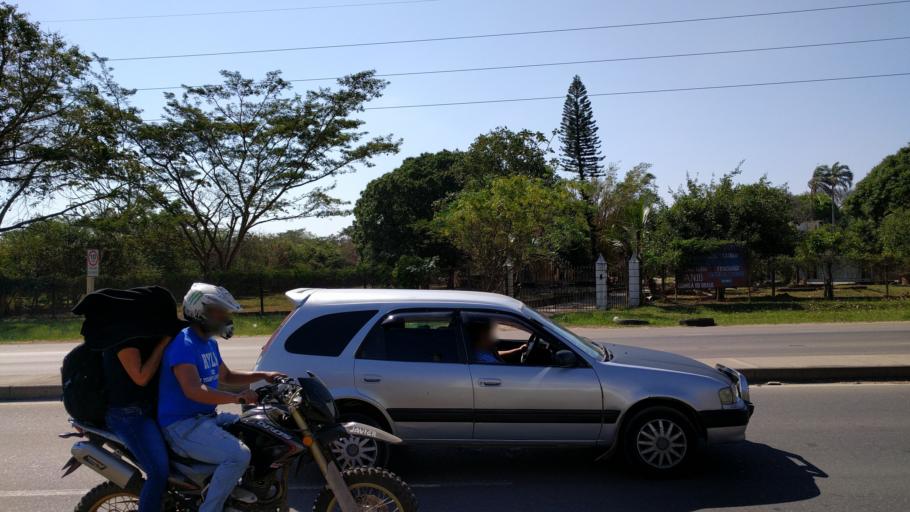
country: BO
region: Santa Cruz
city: Cotoca
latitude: -17.7649
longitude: -63.0770
